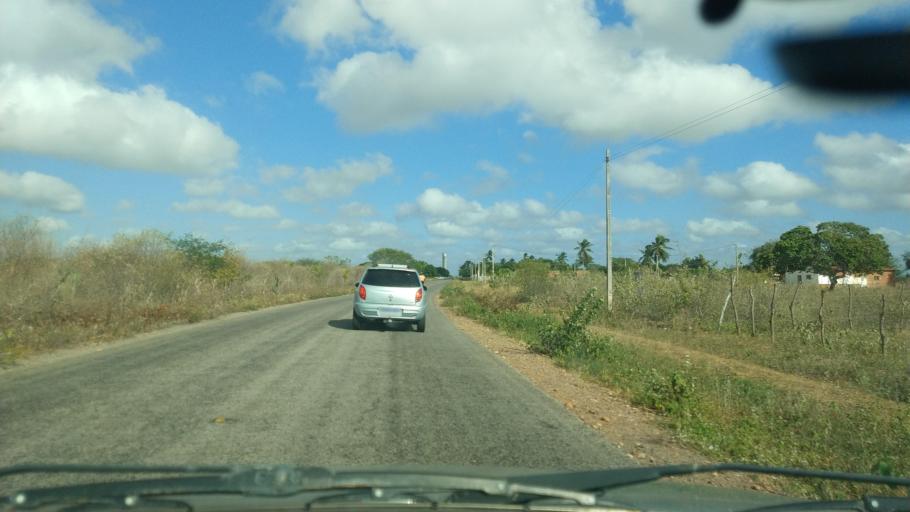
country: BR
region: Rio Grande do Norte
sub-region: Sao Paulo Do Potengi
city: Sao Paulo do Potengi
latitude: -5.9162
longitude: -35.7218
